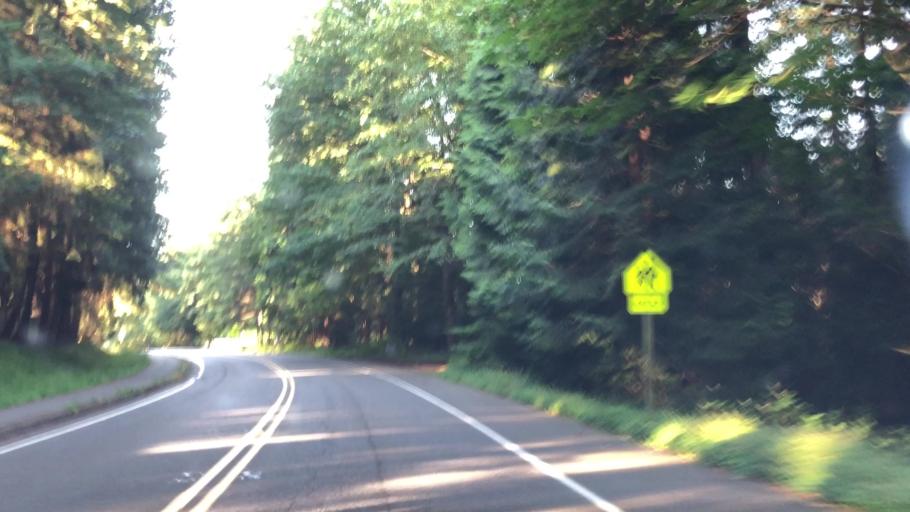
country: US
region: Washington
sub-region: King County
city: Cottage Lake
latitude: 47.7251
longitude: -122.1100
